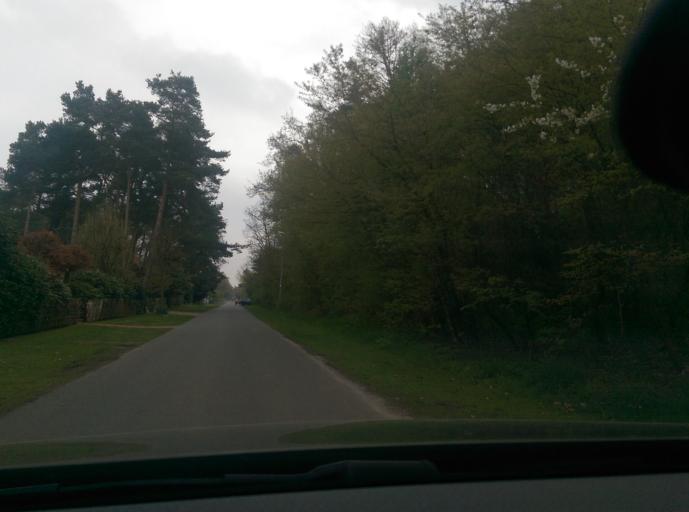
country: DE
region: Lower Saxony
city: Essel
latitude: 52.6667
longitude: 9.7083
